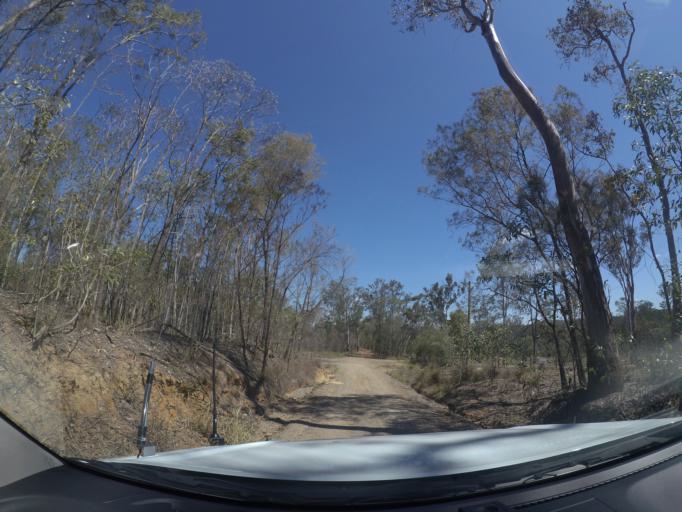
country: AU
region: Queensland
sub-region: Logan
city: North Maclean
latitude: -27.7757
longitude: 152.9370
